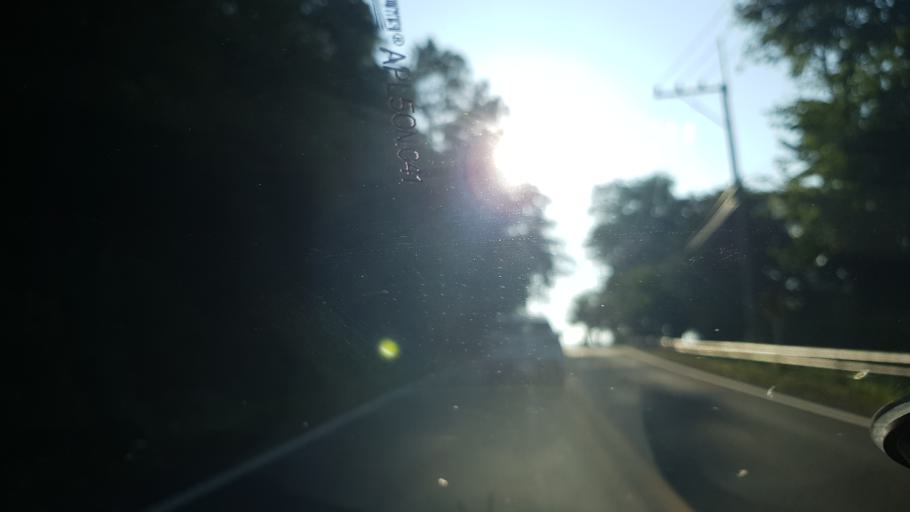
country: TH
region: Chiang Rai
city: Mae Fa Luang
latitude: 20.3078
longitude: 99.8180
